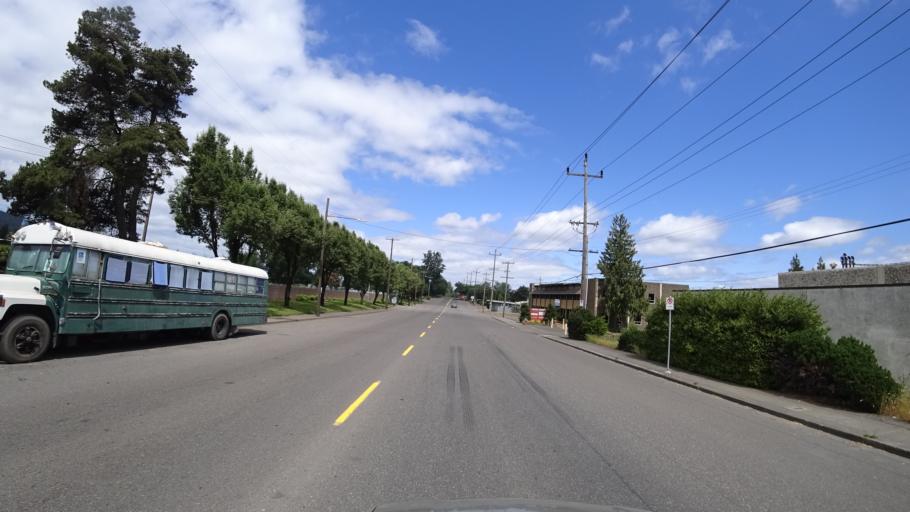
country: US
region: Oregon
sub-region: Washington County
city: West Haven
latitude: 45.6044
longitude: -122.7651
